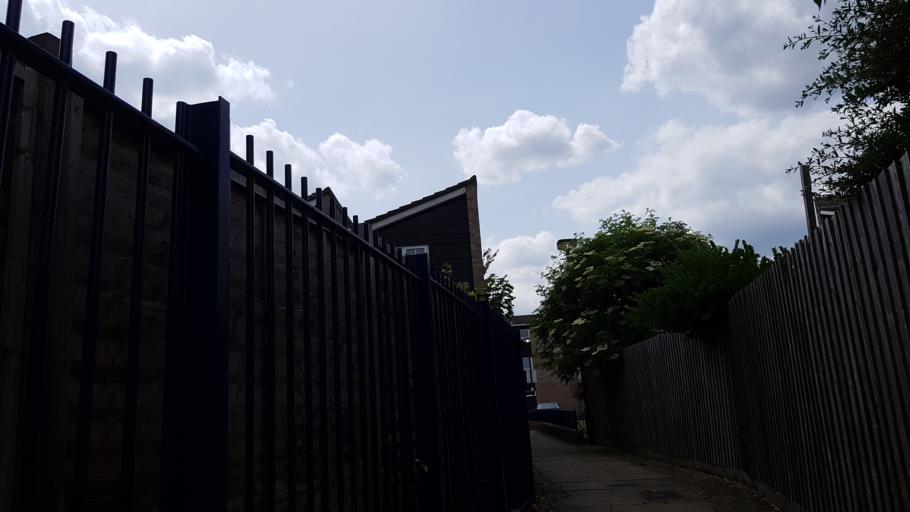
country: GB
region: England
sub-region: Greater London
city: Hackney
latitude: 51.5356
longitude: -0.0280
